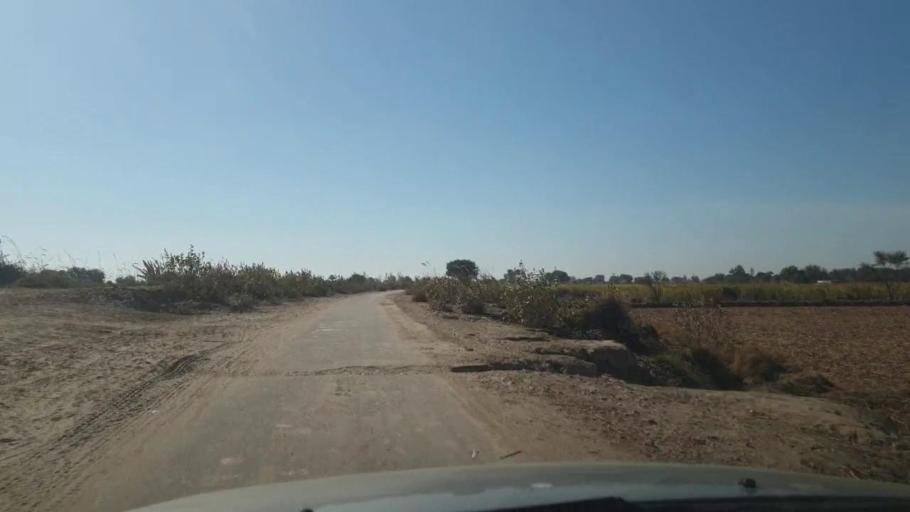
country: PK
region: Sindh
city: Ghotki
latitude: 28.0193
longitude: 69.2678
